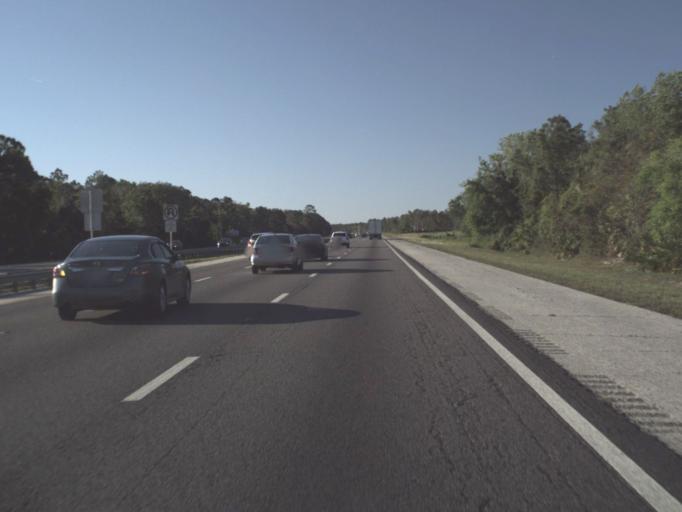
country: US
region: Florida
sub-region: Flagler County
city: Palm Coast
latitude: 29.5257
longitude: -81.2026
